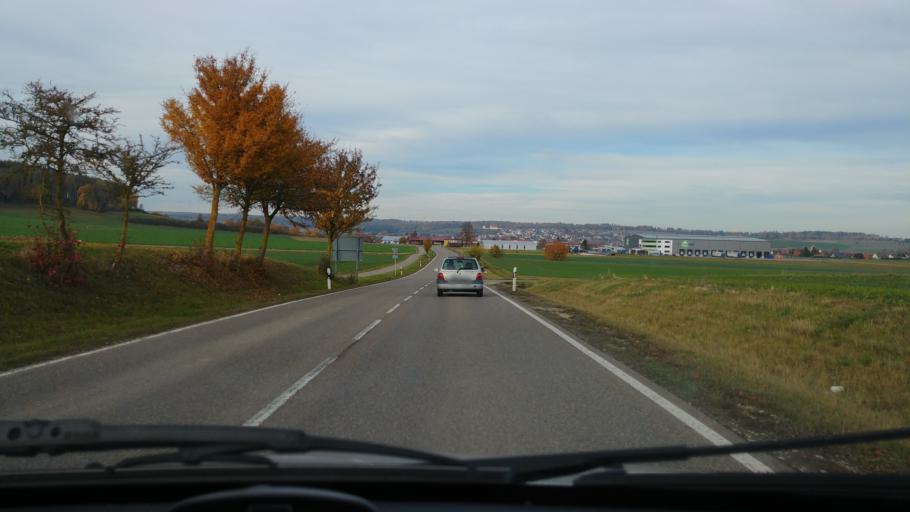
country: DE
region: Bavaria
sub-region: Swabia
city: Bachhagel
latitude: 48.6318
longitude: 10.2946
